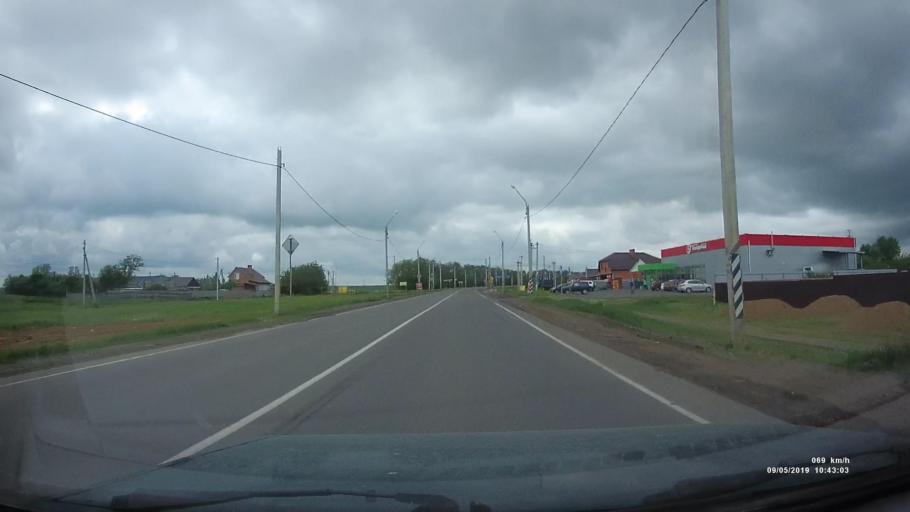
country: RU
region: Rostov
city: Peshkovo
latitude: 47.0120
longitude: 39.4039
